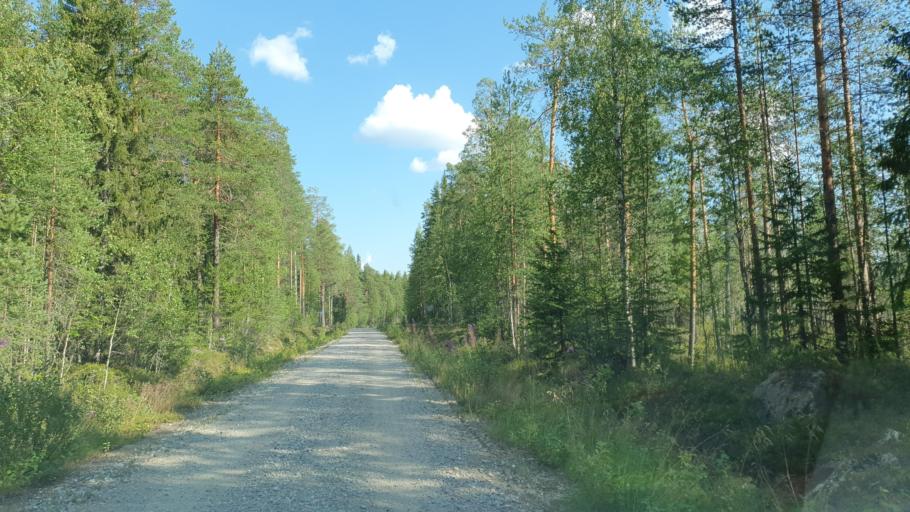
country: FI
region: Kainuu
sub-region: Kehys-Kainuu
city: Kuhmo
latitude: 63.9639
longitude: 29.5485
